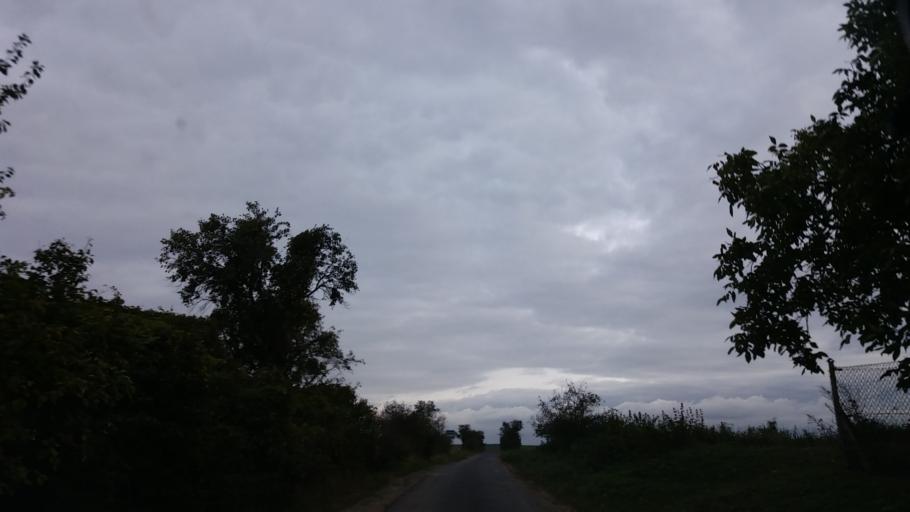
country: PL
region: West Pomeranian Voivodeship
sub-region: Powiat choszczenski
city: Pelczyce
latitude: 53.0355
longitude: 15.3151
